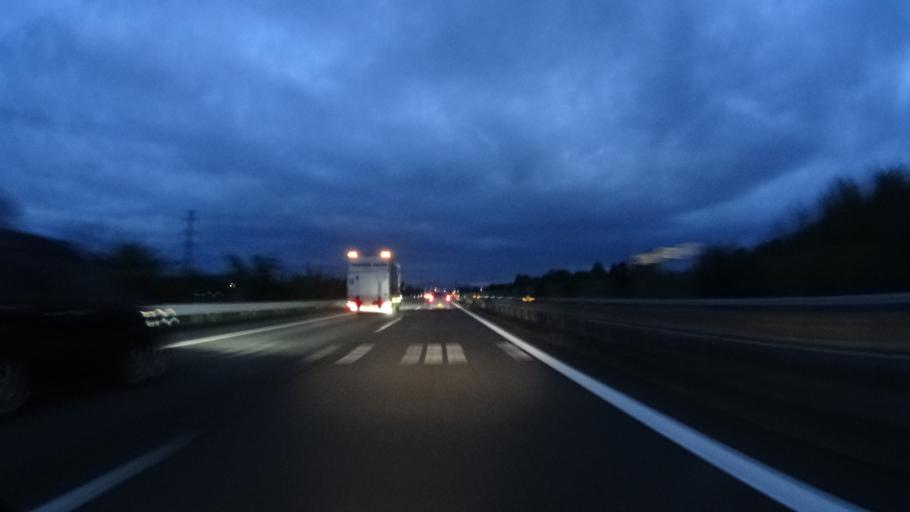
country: JP
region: Shiga Prefecture
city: Youkaichi
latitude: 35.1227
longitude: 136.2679
